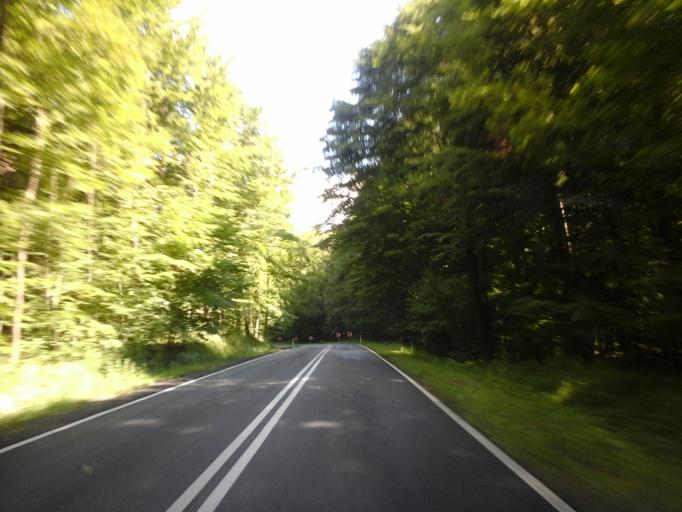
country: PL
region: West Pomeranian Voivodeship
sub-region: Powiat lobeski
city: Wegorzyno
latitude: 53.4871
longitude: 15.5807
